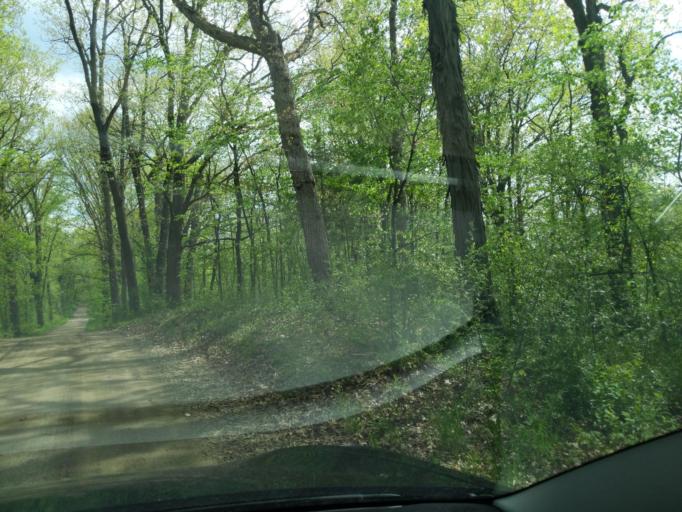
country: US
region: Michigan
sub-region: Washtenaw County
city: Chelsea
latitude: 42.4000
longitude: -84.0545
